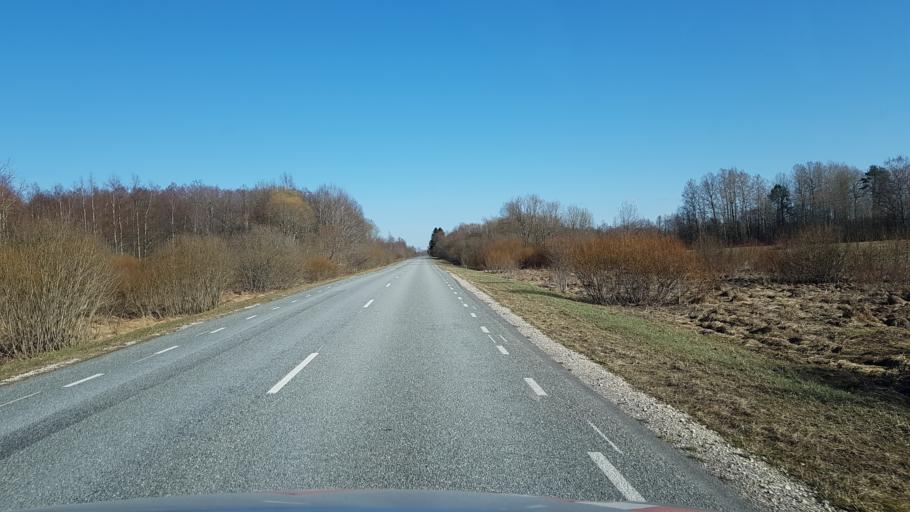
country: EE
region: Laeaene-Virumaa
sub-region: Haljala vald
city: Haljala
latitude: 59.5073
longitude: 26.1131
